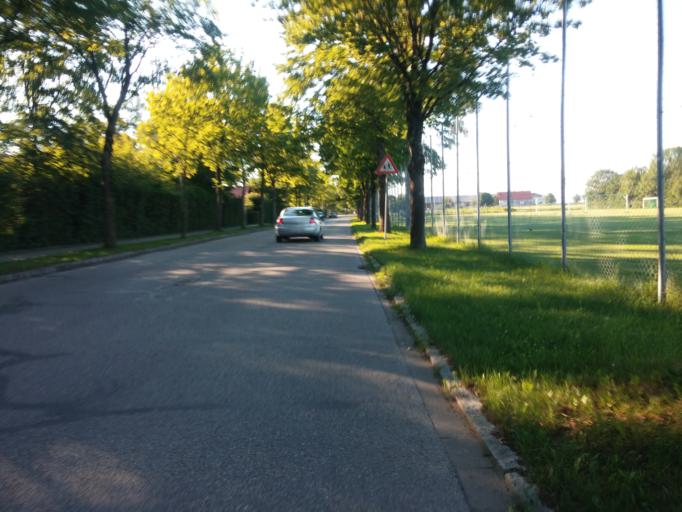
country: DE
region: Bavaria
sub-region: Upper Bavaria
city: Vaterstetten
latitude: 48.1091
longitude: 11.7851
